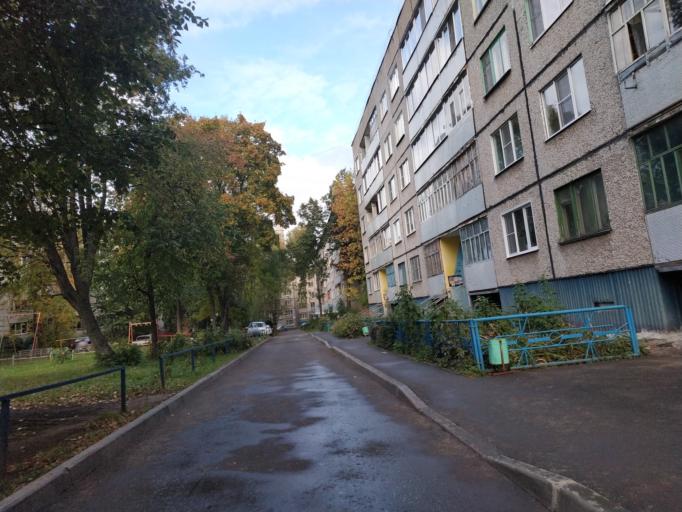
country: RU
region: Chuvashia
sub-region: Cheboksarskiy Rayon
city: Cheboksary
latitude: 56.1435
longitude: 47.1921
